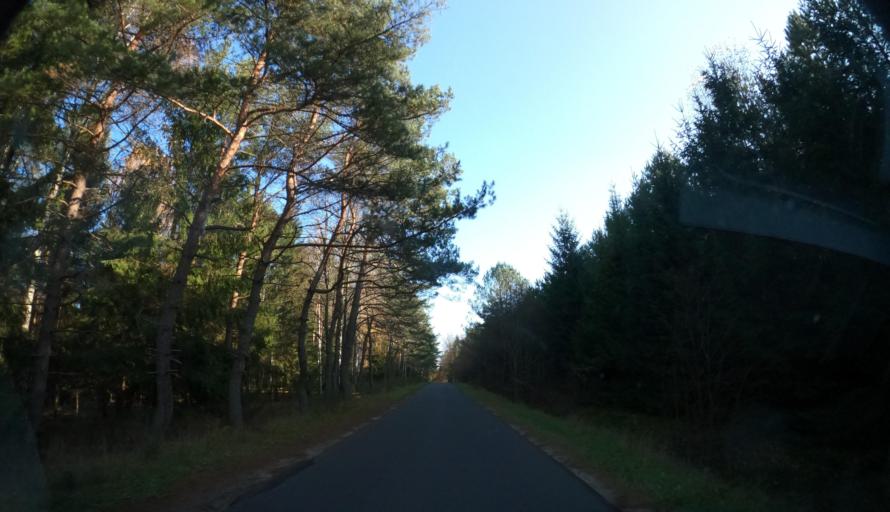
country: PL
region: Pomeranian Voivodeship
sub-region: Powiat slupski
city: Kepice
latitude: 54.2326
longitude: 16.7580
